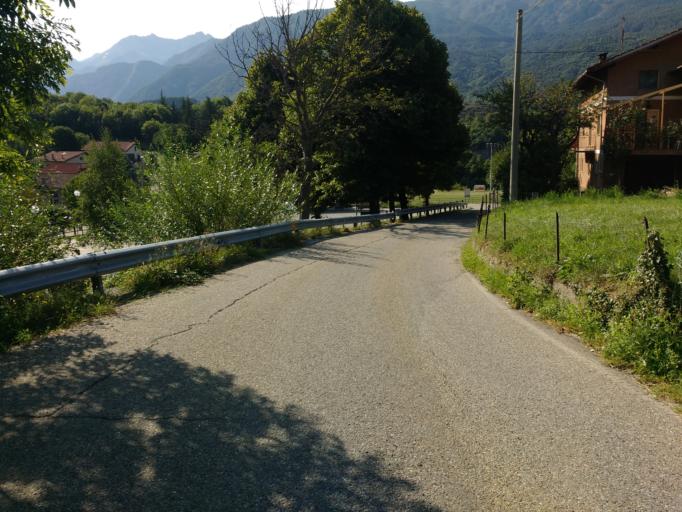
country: IT
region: Piedmont
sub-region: Provincia di Torino
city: Giaglione
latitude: 45.1392
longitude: 7.0158
